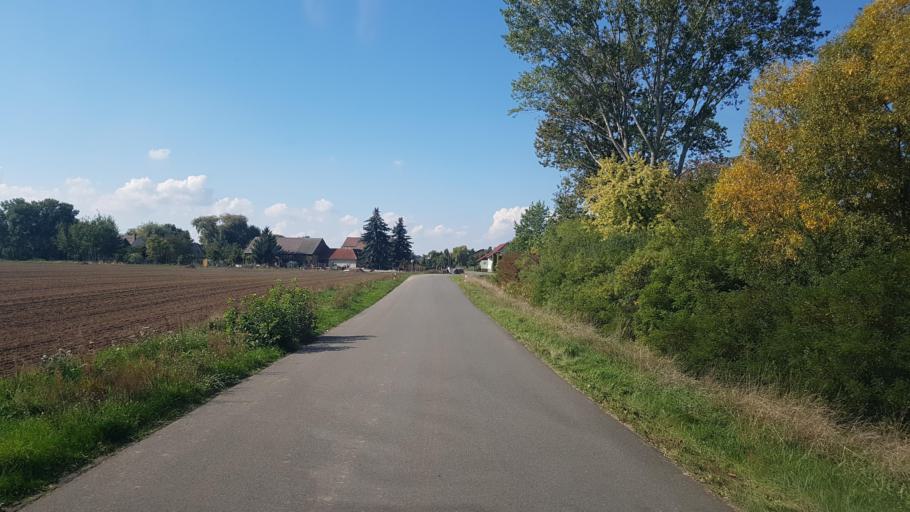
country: DE
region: Brandenburg
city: Ihlow
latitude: 51.8324
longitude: 13.3662
